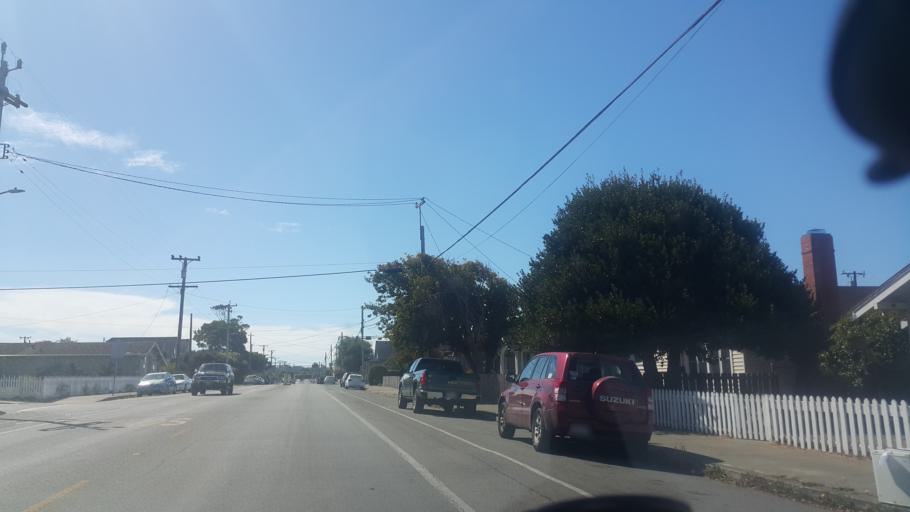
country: US
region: California
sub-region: Mendocino County
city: Fort Bragg
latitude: 39.4439
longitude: -123.7981
